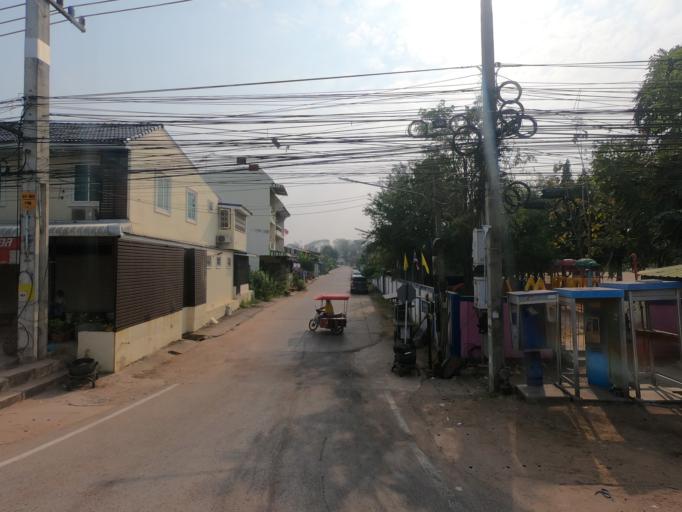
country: TH
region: Khon Kaen
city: Khon Kaen
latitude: 16.3397
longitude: 102.8019
